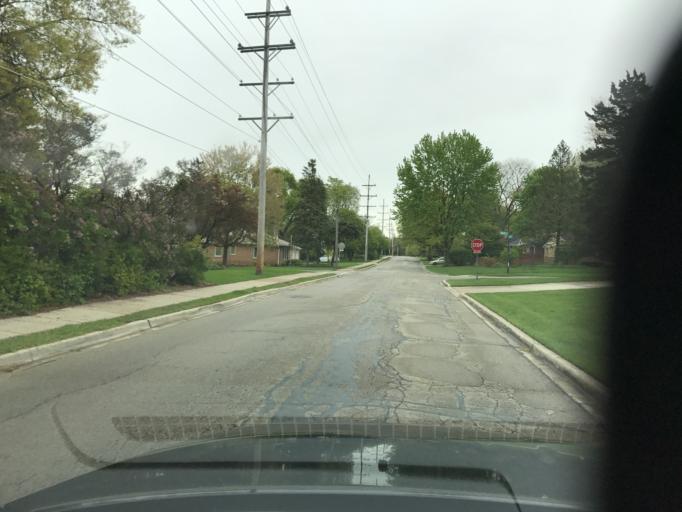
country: US
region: Illinois
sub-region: DuPage County
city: Naperville
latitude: 41.7676
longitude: -88.1402
